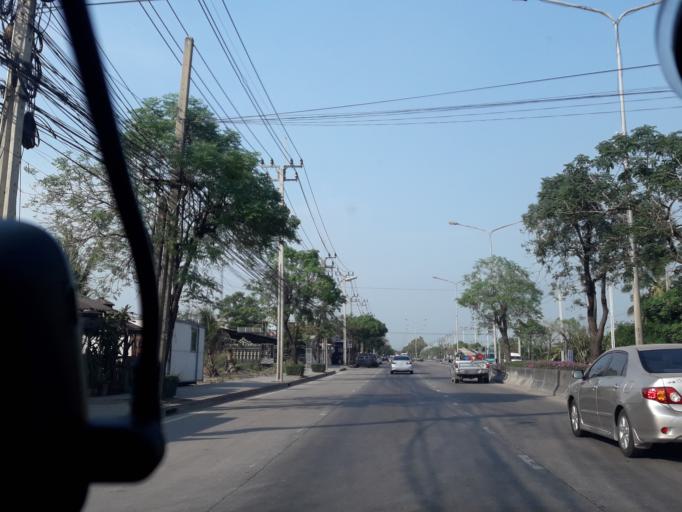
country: TH
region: Bangkok
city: Khlong Sam Wa
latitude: 13.8836
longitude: 100.7317
